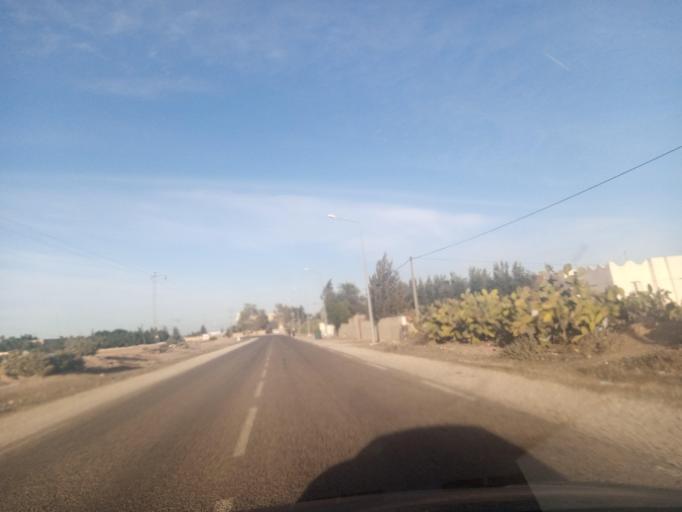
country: TN
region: Al Mahdiyah
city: Shurban
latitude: 34.9583
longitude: 10.3608
